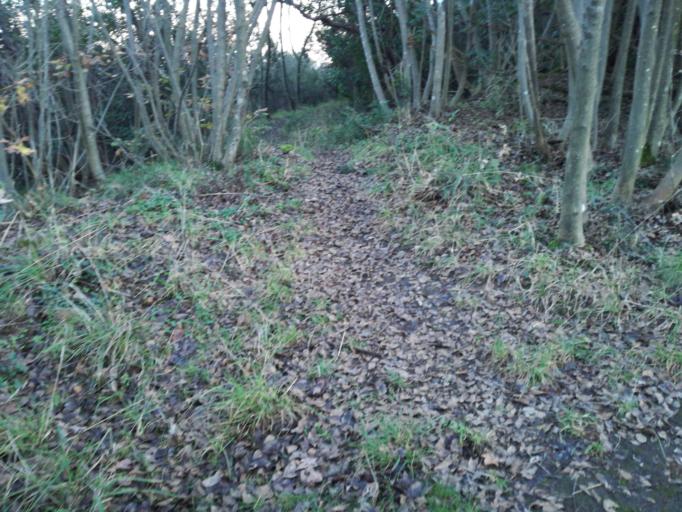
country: IT
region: Veneto
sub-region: Provincia di Padova
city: Battaglia Terme
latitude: 45.3032
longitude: 11.7683
